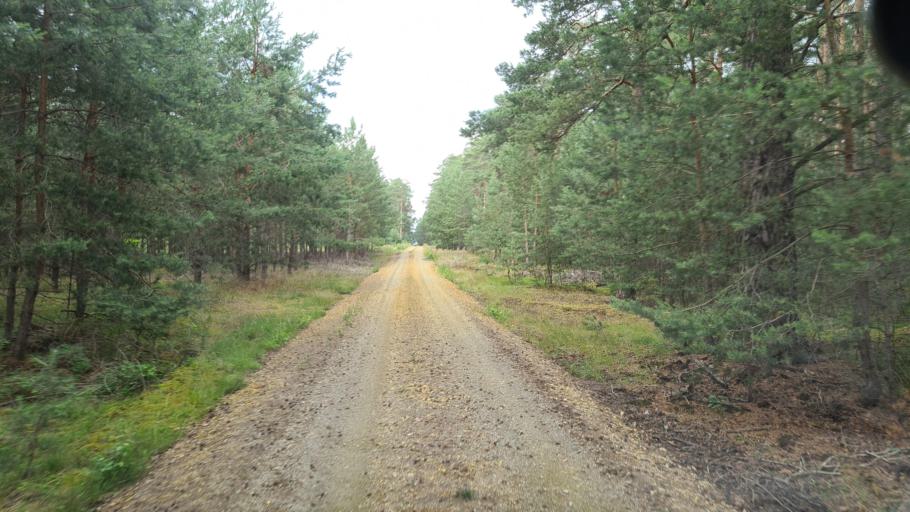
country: DE
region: Brandenburg
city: Bronkow
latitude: 51.6894
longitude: 13.8736
